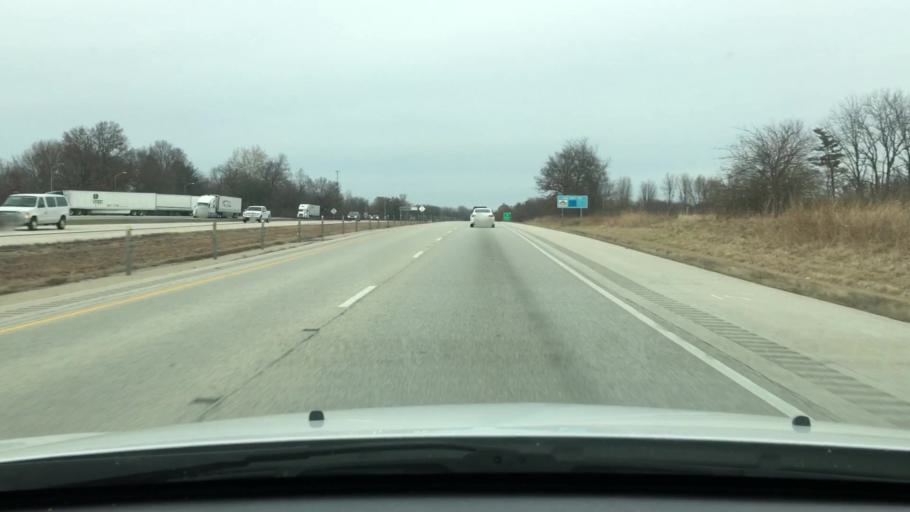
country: US
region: Illinois
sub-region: Sangamon County
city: Sherman
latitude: 39.8856
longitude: -89.5961
